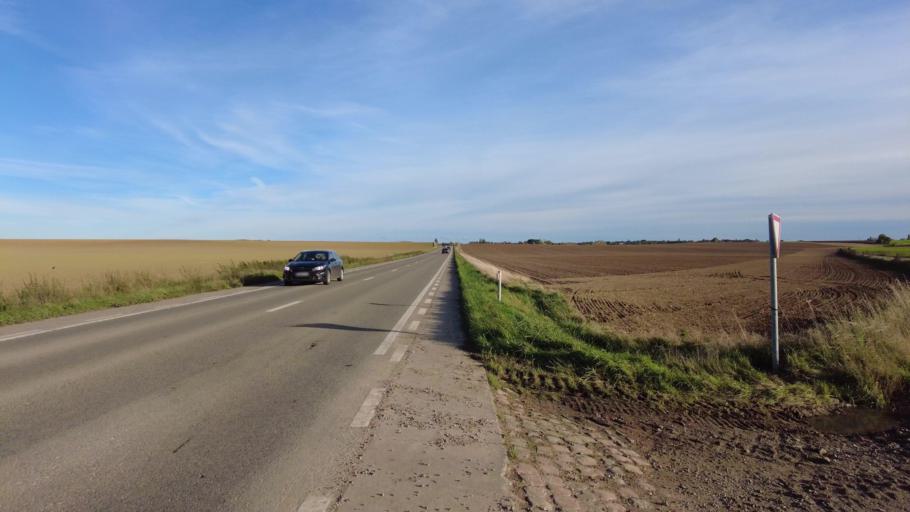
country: BE
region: Wallonia
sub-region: Province du Brabant Wallon
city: Jodoigne
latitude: 50.7108
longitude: 4.9026
